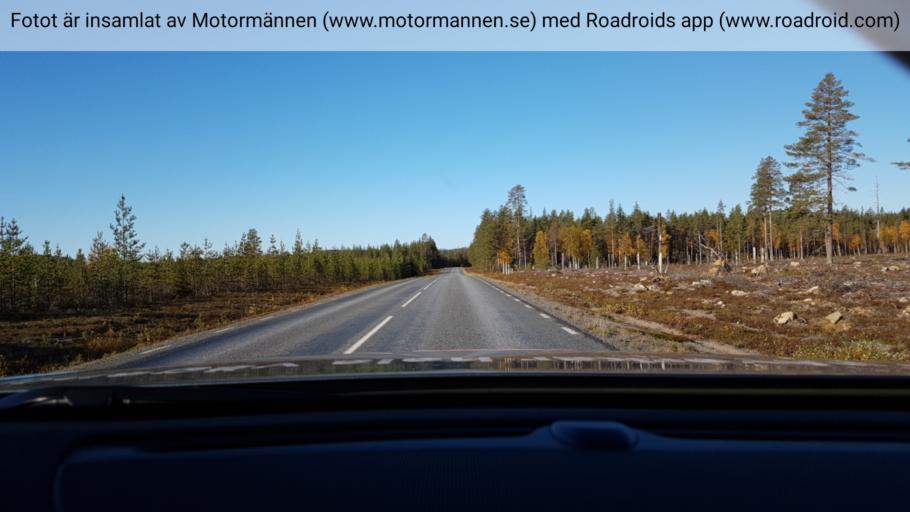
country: SE
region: Vaesterbotten
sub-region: Skelleftea Kommun
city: Boliden
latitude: 65.3820
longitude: 20.1512
